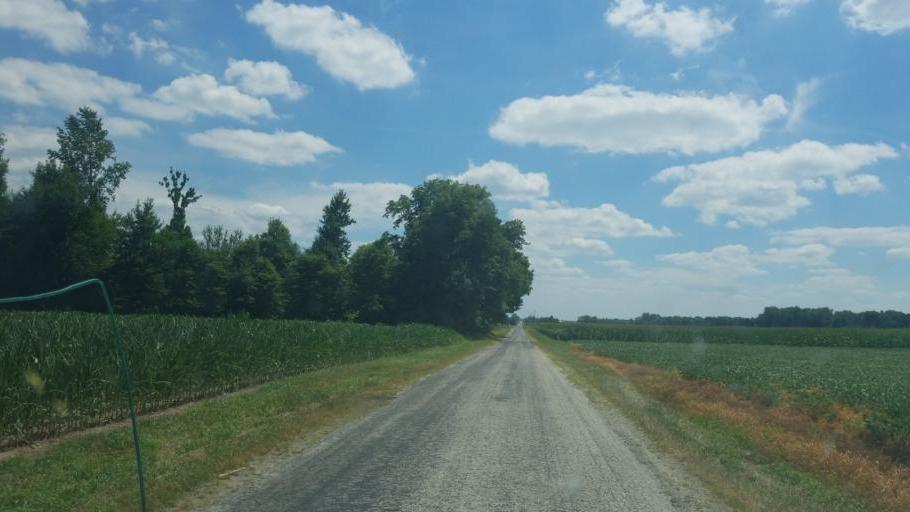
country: US
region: Ohio
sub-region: Defiance County
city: Hicksville
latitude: 41.3476
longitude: -84.6901
